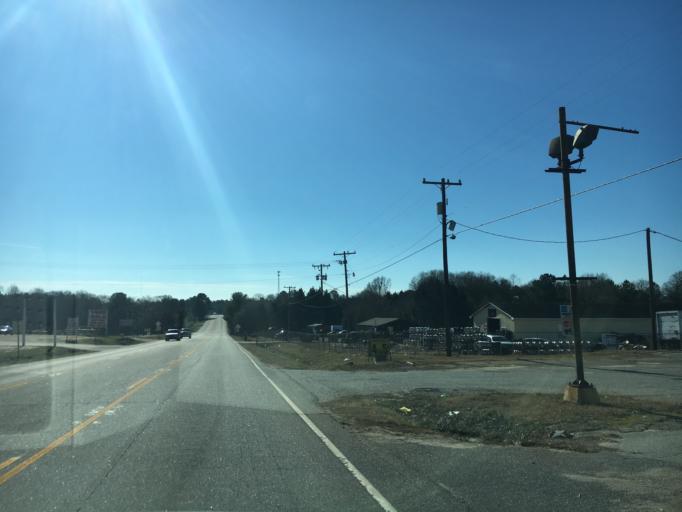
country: US
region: South Carolina
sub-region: Anderson County
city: Williamston
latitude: 34.5850
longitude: -82.5506
